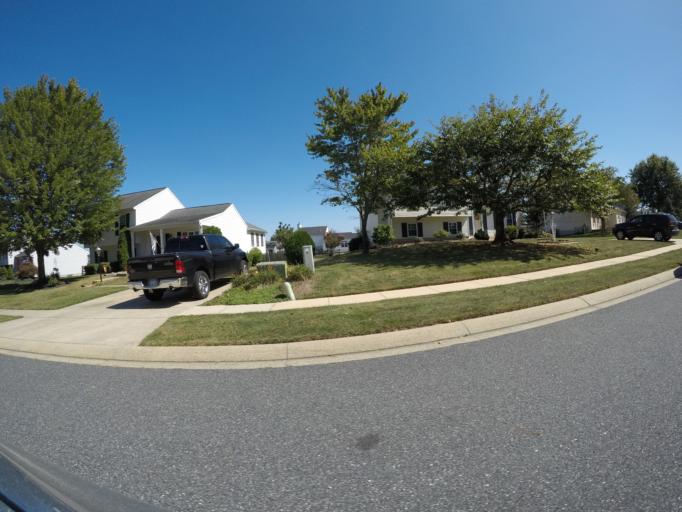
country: US
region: Maryland
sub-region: Harford County
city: Riverside
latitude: 39.4750
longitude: -76.2816
